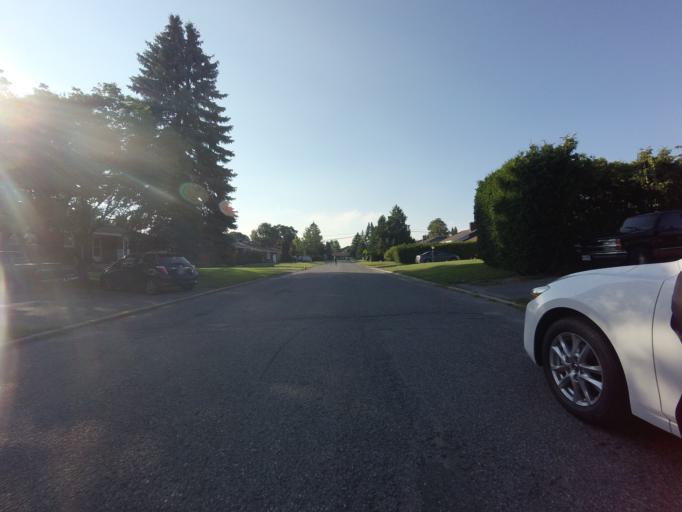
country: CA
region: Ontario
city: Bells Corners
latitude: 45.3266
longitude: -75.7623
